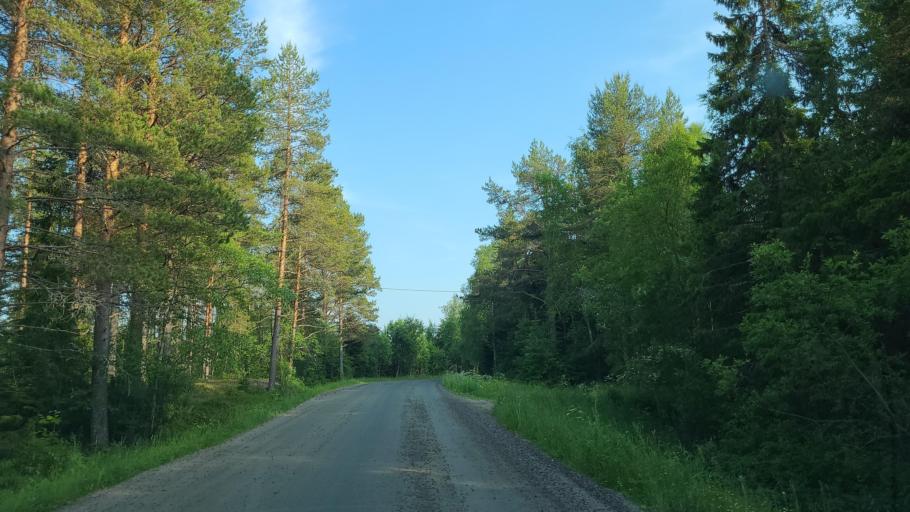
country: SE
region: Vaesterbotten
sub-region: Skelleftea Kommun
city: Burea
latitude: 64.4399
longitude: 21.5000
